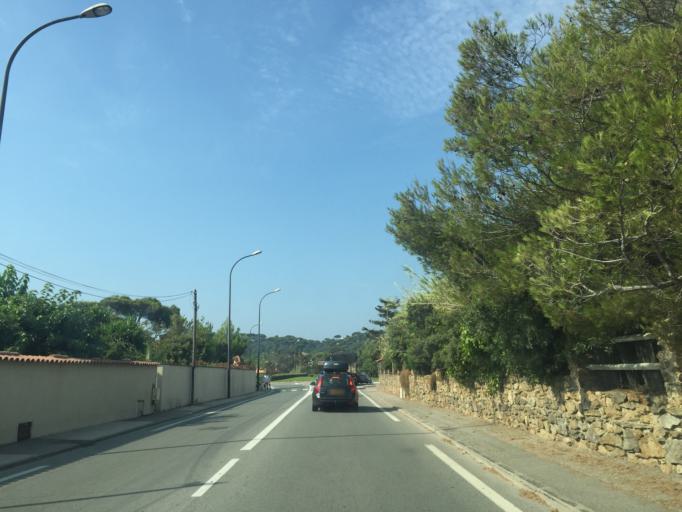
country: FR
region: Provence-Alpes-Cote d'Azur
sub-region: Departement du Var
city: Sainte-Maxime
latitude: 43.3241
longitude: 6.6642
